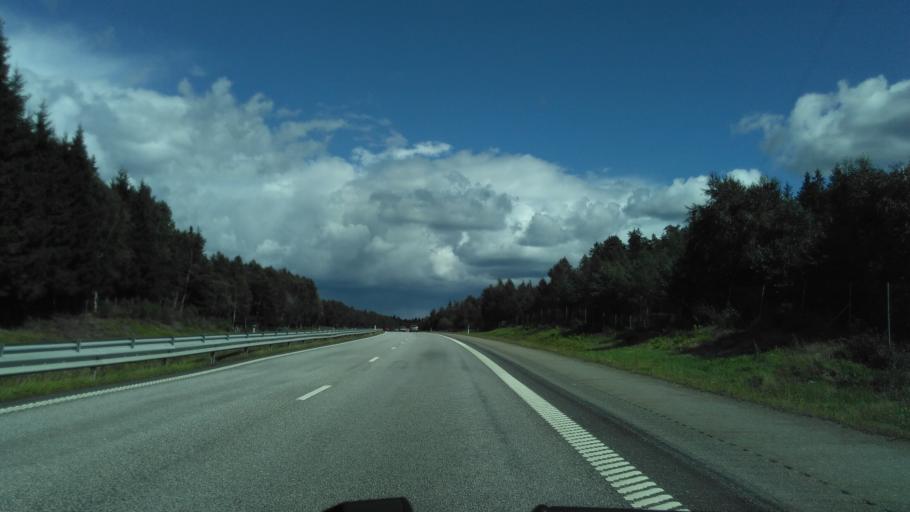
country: SE
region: Vaestra Goetaland
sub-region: Harryda Kommun
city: Hindas
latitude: 57.6676
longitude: 12.4138
